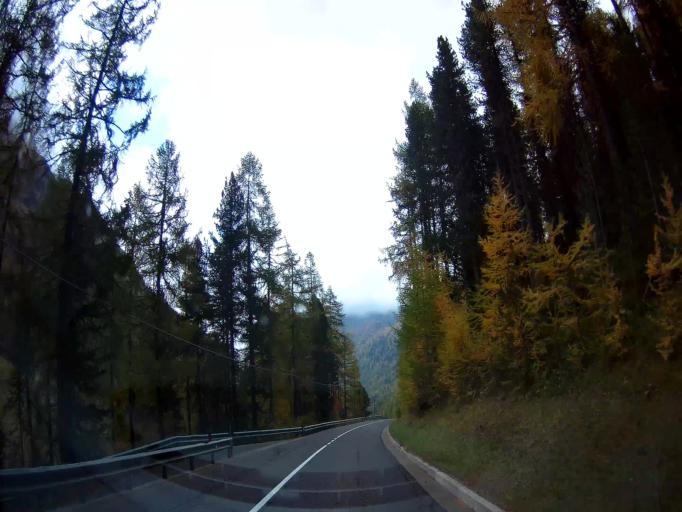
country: IT
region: Trentino-Alto Adige
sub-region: Bolzano
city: Silandro
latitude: 46.7396
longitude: 10.7922
